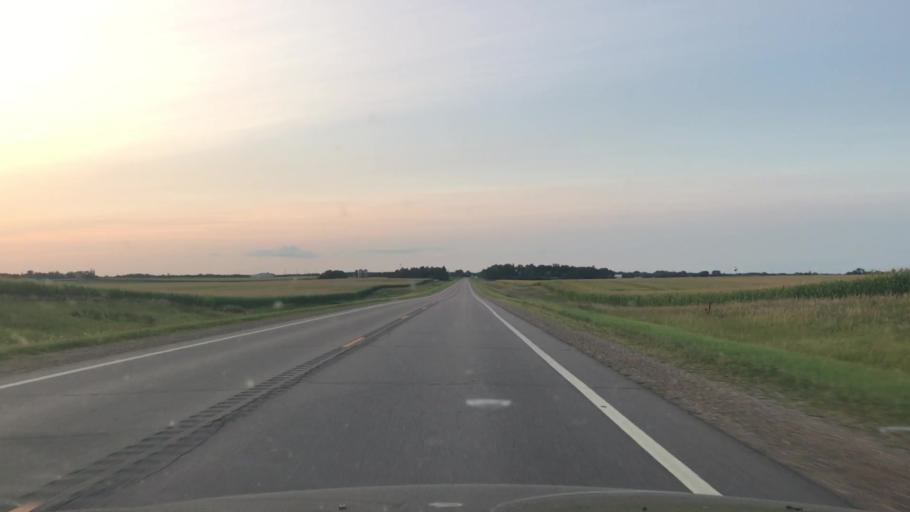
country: US
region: Minnesota
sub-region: Redwood County
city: Redwood Falls
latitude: 44.5082
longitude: -95.1179
